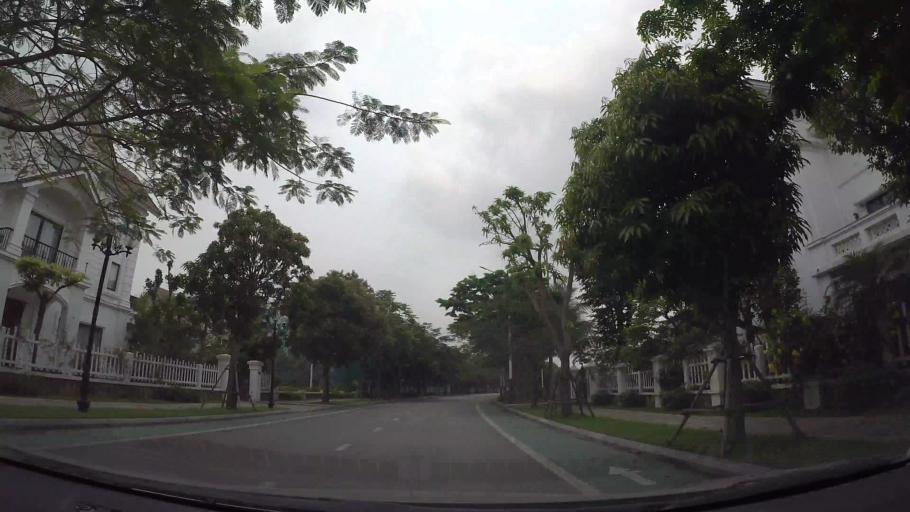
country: VN
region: Ha Noi
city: Trau Quy
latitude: 21.0546
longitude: 105.9132
